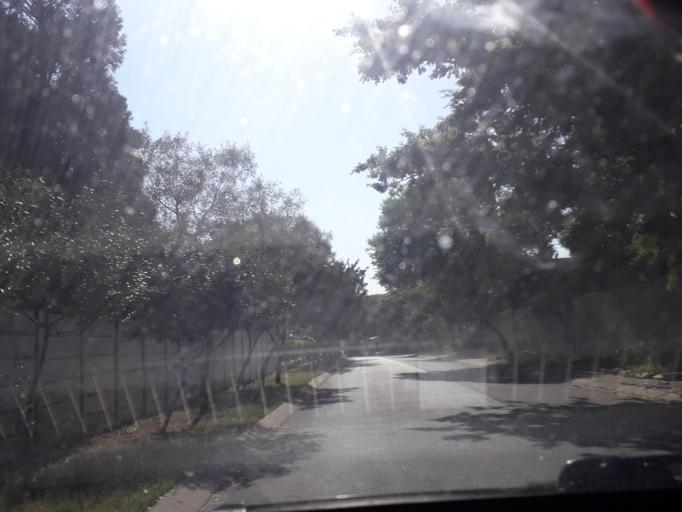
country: ZA
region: Gauteng
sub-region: City of Johannesburg Metropolitan Municipality
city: Midrand
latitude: -26.0203
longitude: 28.0671
